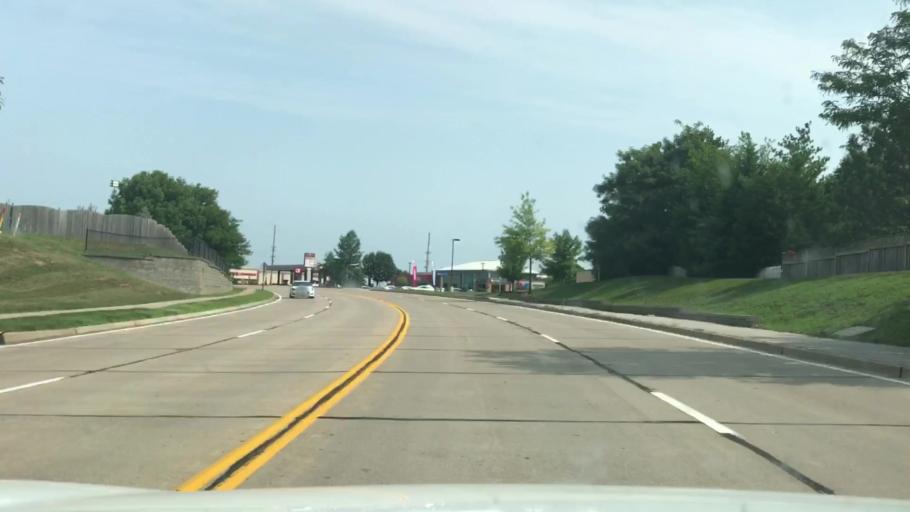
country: US
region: Missouri
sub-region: Saint Charles County
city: Dardenne Prairie
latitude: 38.7709
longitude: -90.7381
